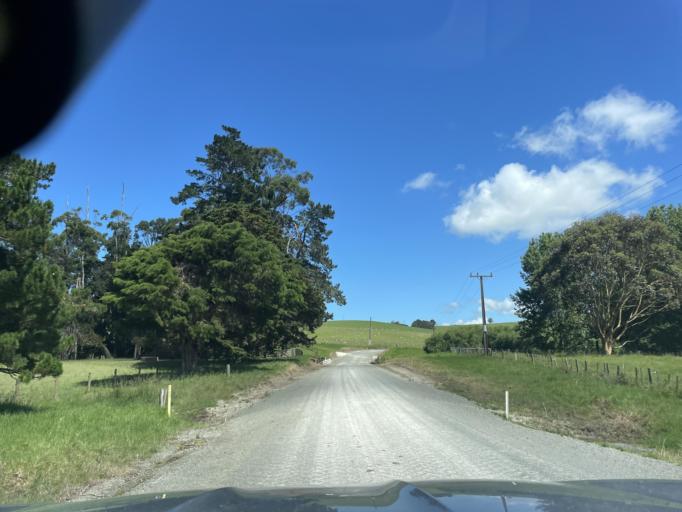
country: NZ
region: Auckland
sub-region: Auckland
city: Wellsford
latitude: -36.2869
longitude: 174.3284
